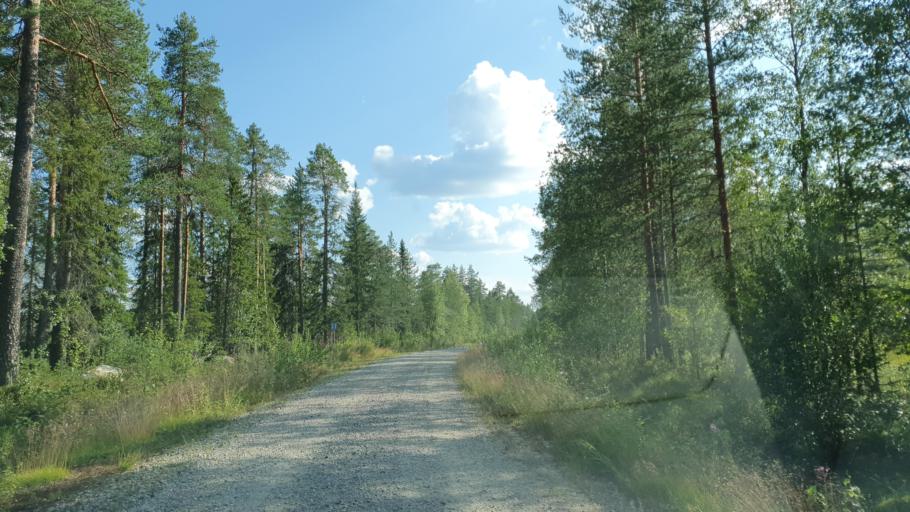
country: FI
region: Kainuu
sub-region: Kehys-Kainuu
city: Kuhmo
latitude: 63.9612
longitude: 29.5541
